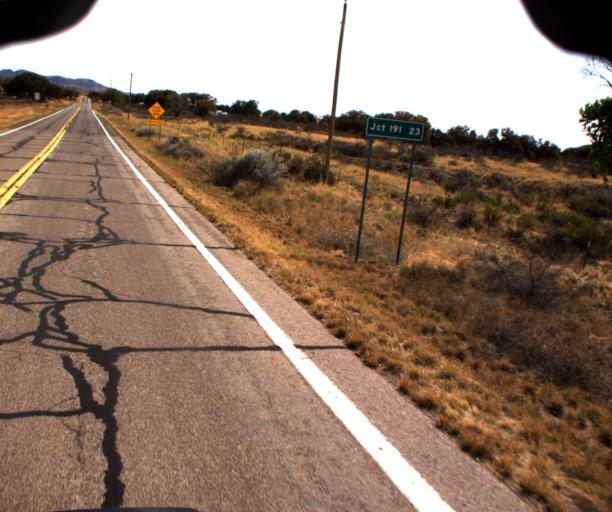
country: US
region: Arizona
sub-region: Cochise County
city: Willcox
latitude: 32.0053
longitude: -109.4400
